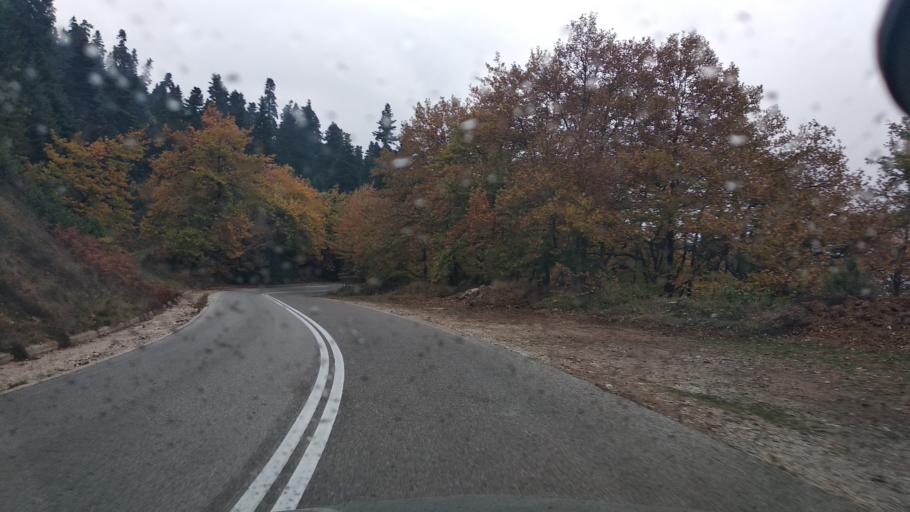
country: GR
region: Thessaly
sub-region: Trikala
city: Pyli
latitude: 39.5169
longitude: 21.5258
